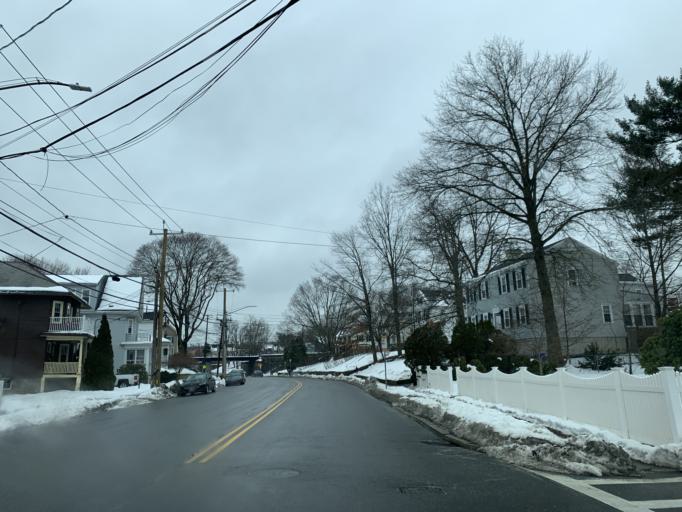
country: US
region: Massachusetts
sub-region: Norfolk County
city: Dedham
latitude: 42.2828
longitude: -71.1609
